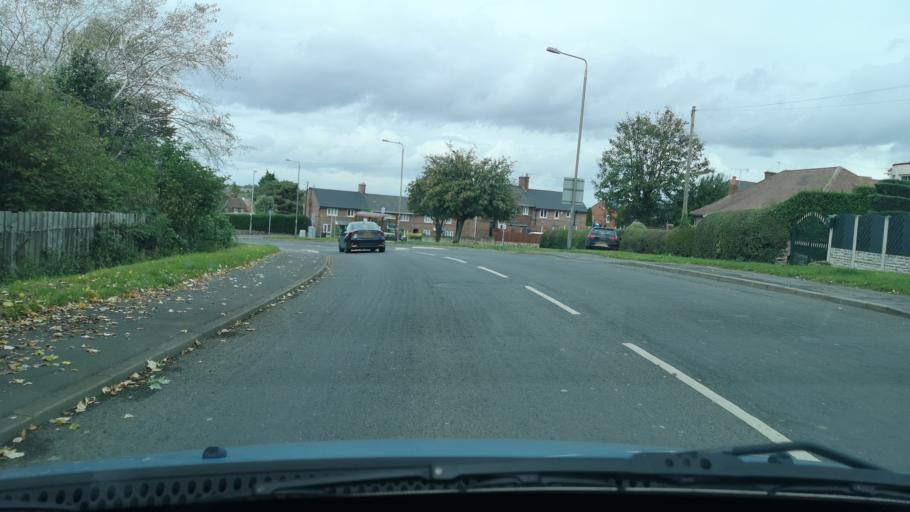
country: GB
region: England
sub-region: City and Borough of Wakefield
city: Featherstone
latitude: 53.6705
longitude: -1.3493
